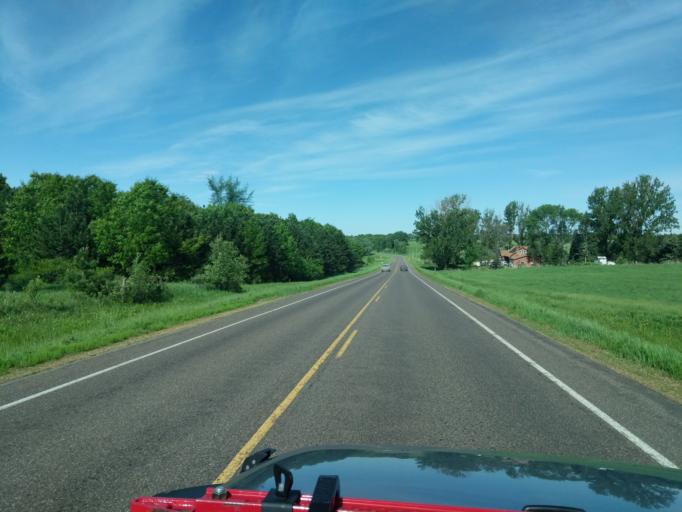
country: US
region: Wisconsin
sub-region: Pierce County
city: River Falls
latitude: 44.8698
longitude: -92.5037
